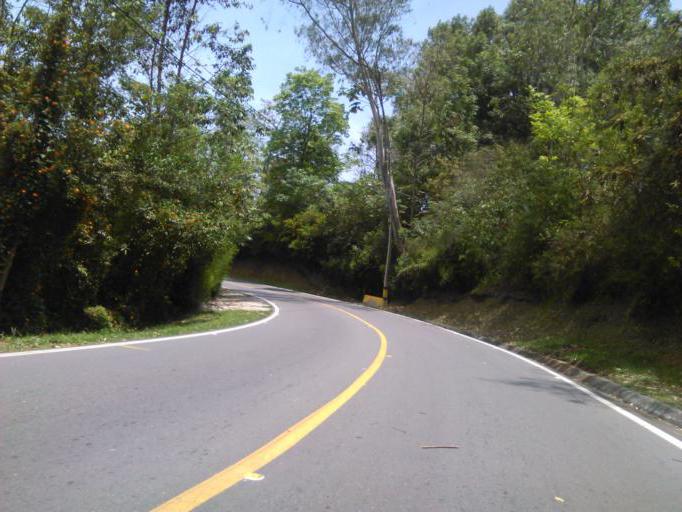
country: CO
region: Antioquia
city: La Ceja
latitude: 6.0089
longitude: -75.4075
